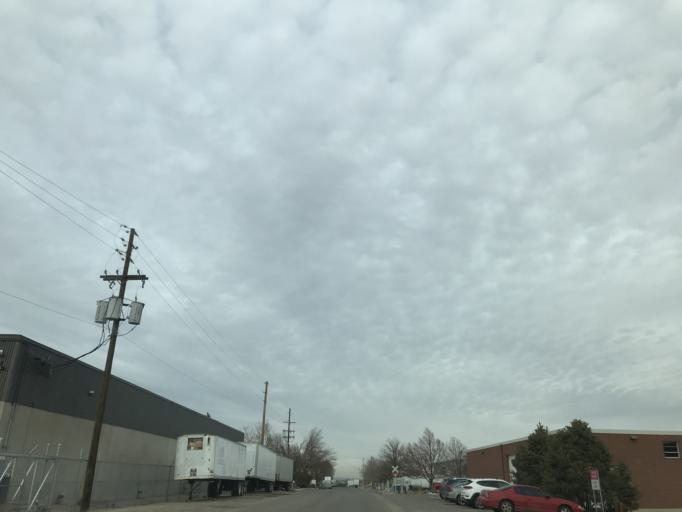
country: US
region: Colorado
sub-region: Adams County
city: Commerce City
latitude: 39.7795
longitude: -104.9159
